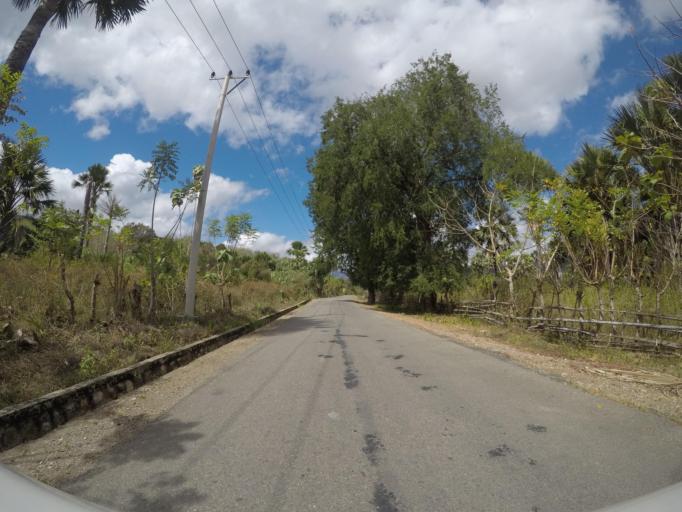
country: TL
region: Lautem
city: Lospalos
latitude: -8.4416
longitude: 126.8263
